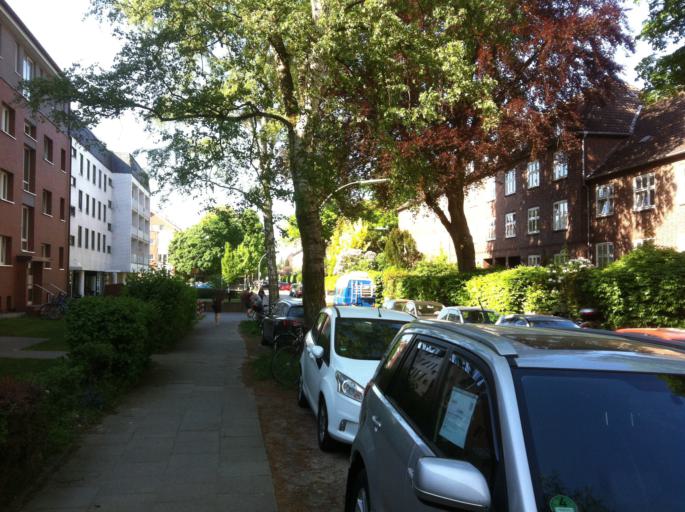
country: DE
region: Hamburg
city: Altona
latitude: 53.5504
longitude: 9.9093
